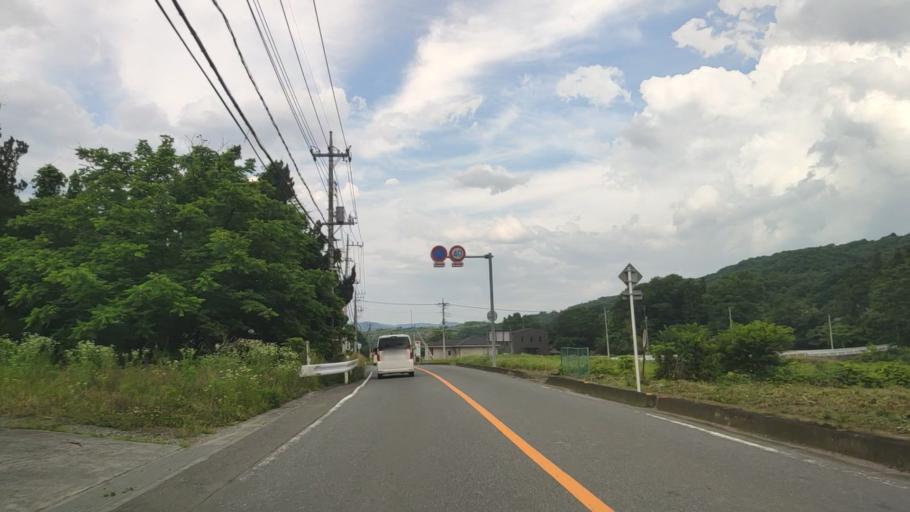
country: JP
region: Saitama
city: Chichibu
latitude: 36.0135
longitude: 139.0550
